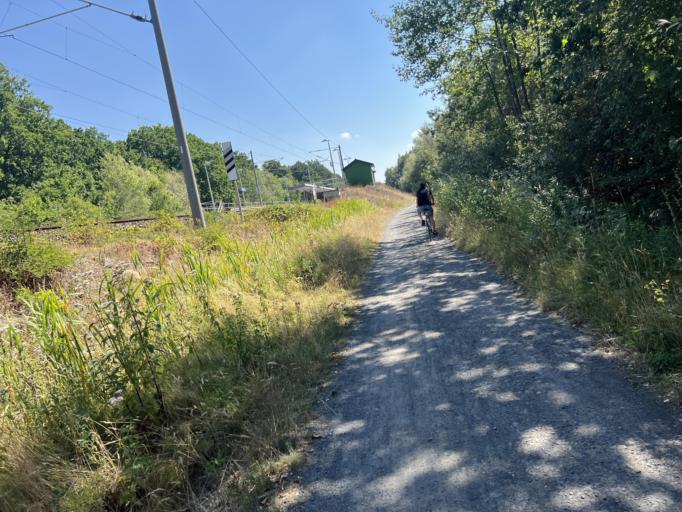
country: DE
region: Hesse
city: Obertshausen
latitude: 50.0819
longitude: 8.8270
